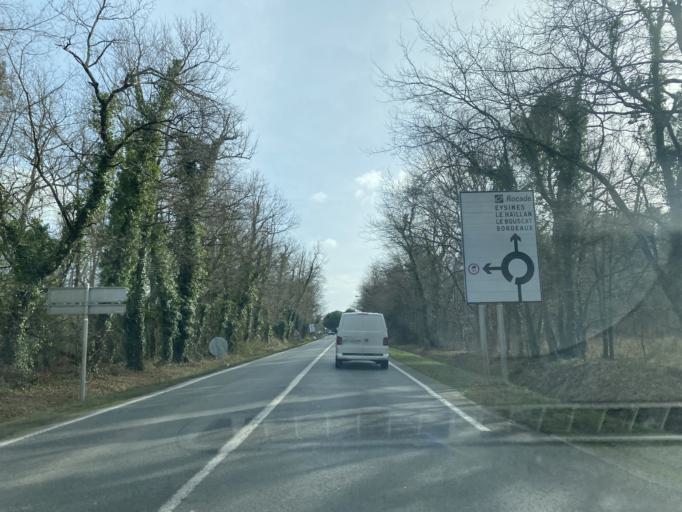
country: FR
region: Aquitaine
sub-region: Departement de la Gironde
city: Le Taillan-Medoc
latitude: 44.9173
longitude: -0.6705
